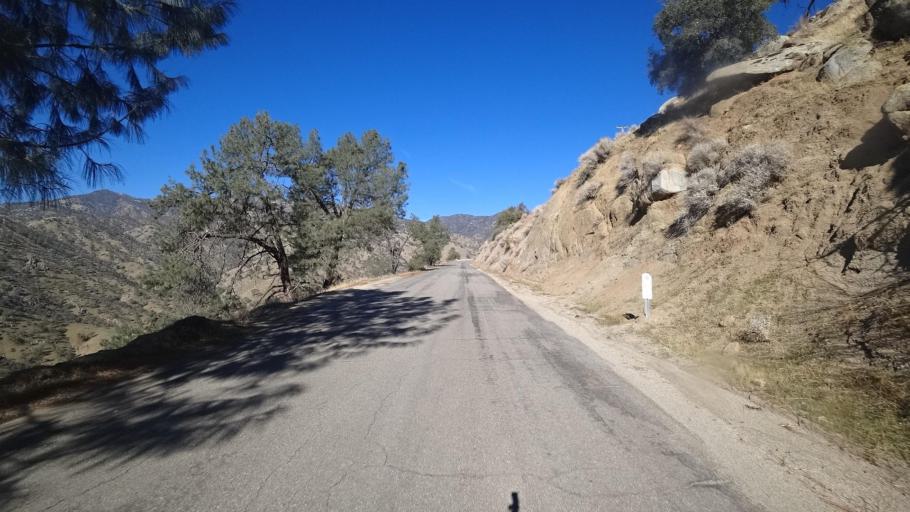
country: US
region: California
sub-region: Kern County
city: Bodfish
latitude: 35.5468
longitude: -118.6112
